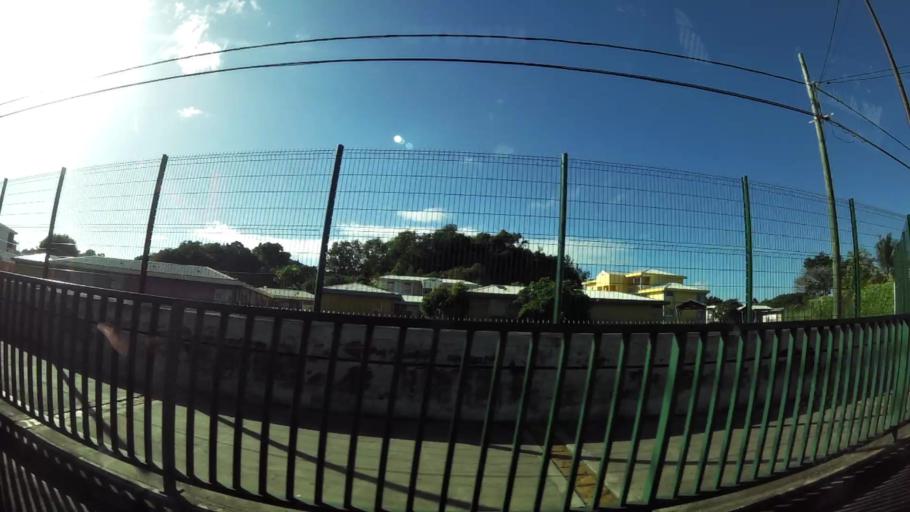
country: GP
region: Guadeloupe
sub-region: Guadeloupe
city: Petit-Canal
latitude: 16.3286
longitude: -61.4502
